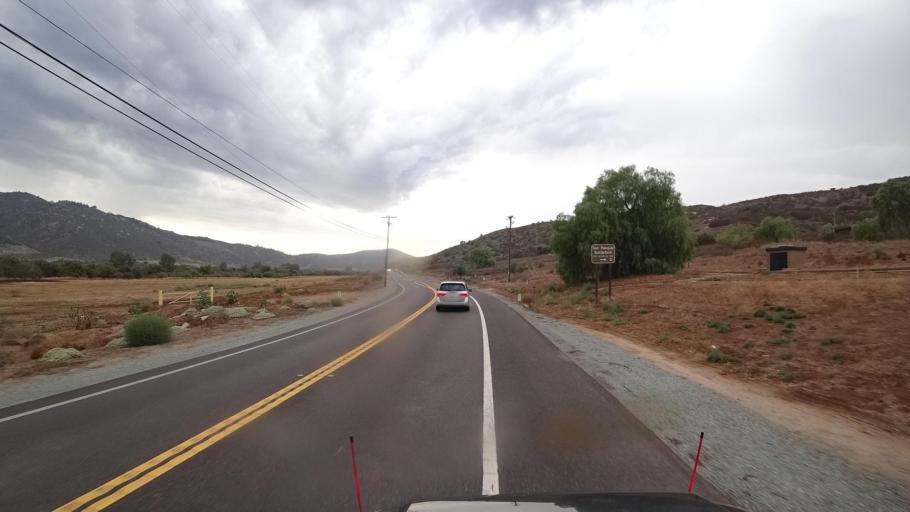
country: US
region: California
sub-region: San Diego County
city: San Pasqual
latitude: 33.0886
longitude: -116.9817
